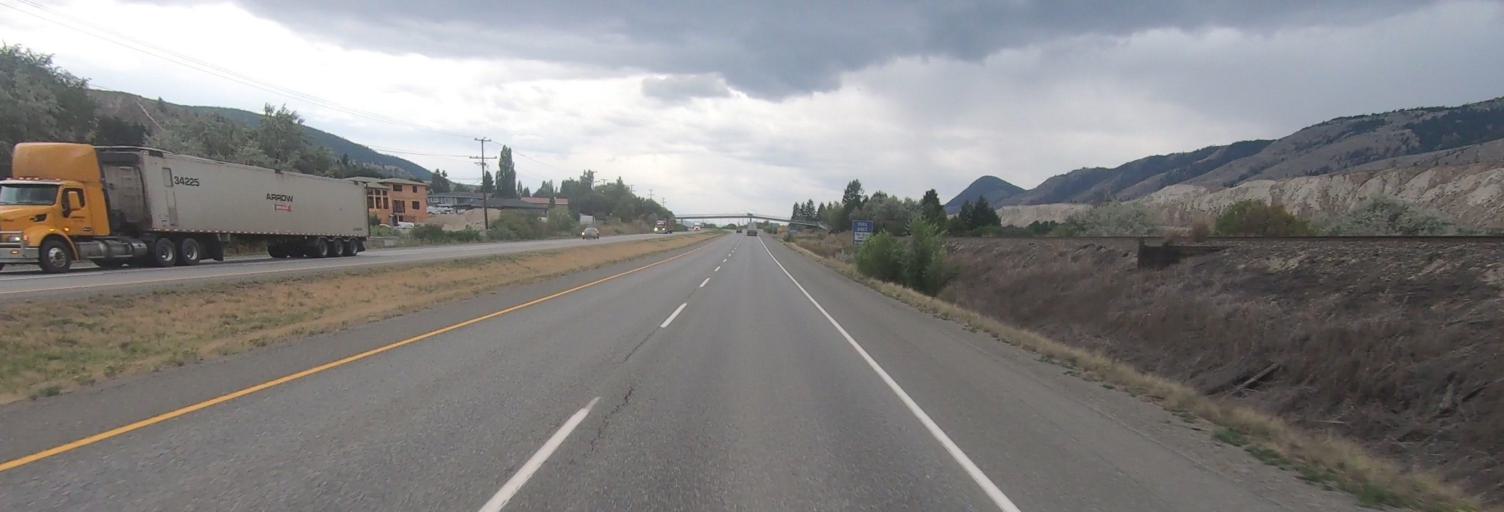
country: CA
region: British Columbia
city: Kamloops
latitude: 50.6694
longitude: -120.1718
